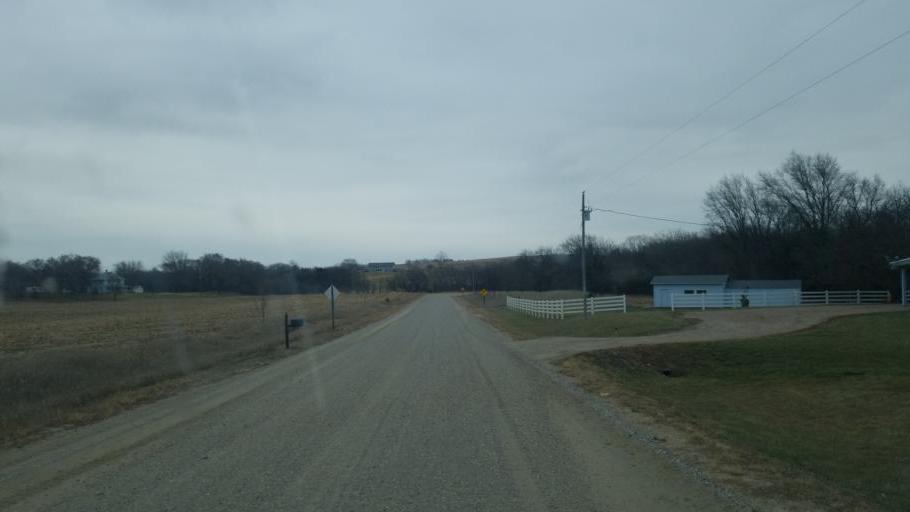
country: US
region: South Dakota
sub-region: Yankton County
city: Yankton
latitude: 42.7870
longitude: -97.3740
